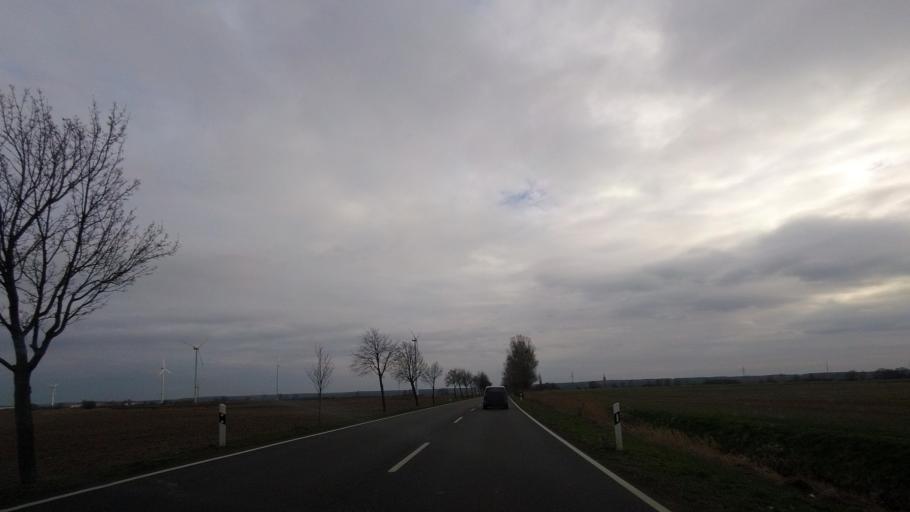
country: DE
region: Saxony-Anhalt
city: Kemberg
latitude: 51.7945
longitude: 12.6513
